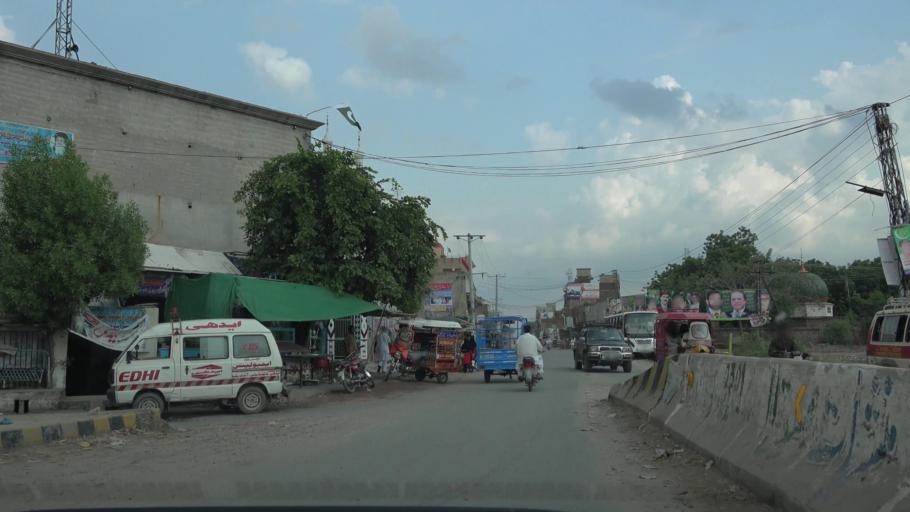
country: PK
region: Punjab
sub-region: Nankana Sahib District
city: Shahkot
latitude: 31.5777
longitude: 73.4808
